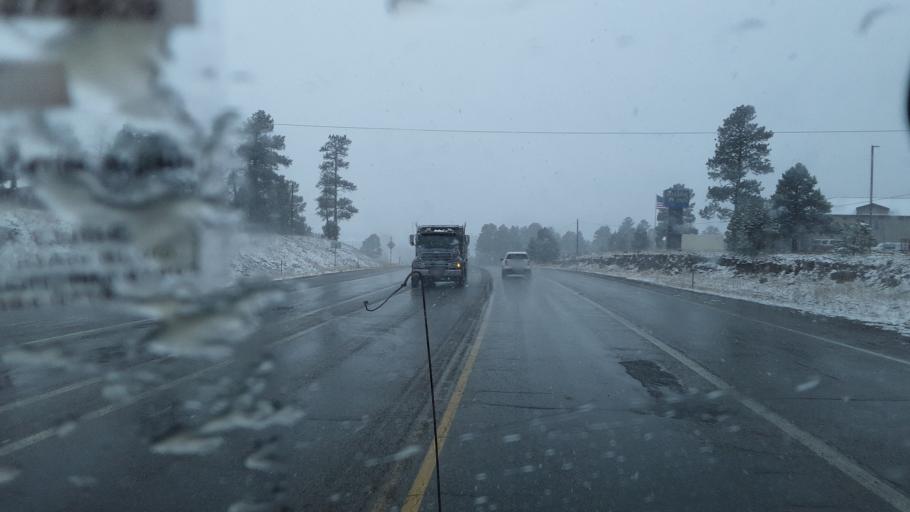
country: US
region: Colorado
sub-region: Archuleta County
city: Pagosa Springs
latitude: 37.2675
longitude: -107.0531
